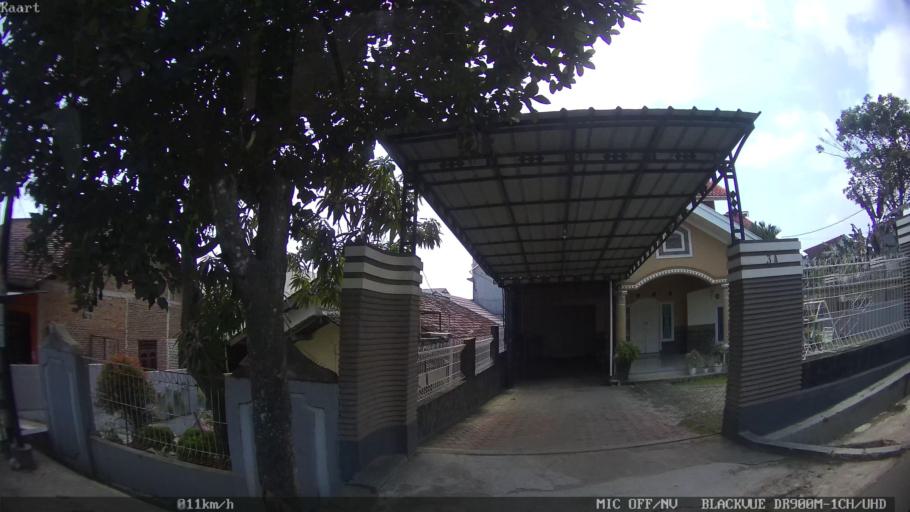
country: ID
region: Lampung
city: Kedaton
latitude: -5.3645
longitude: 105.2679
